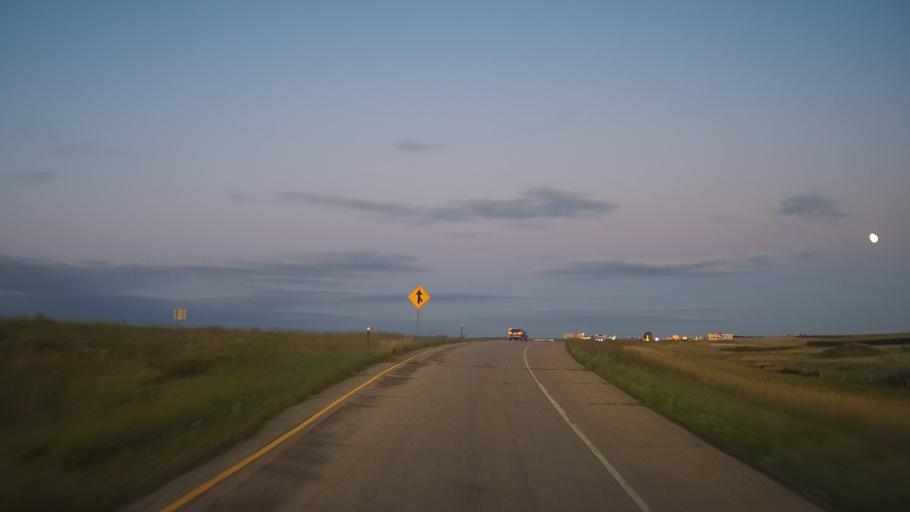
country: US
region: South Dakota
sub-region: Lyman County
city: Kennebec
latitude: 43.8632
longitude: -99.6039
